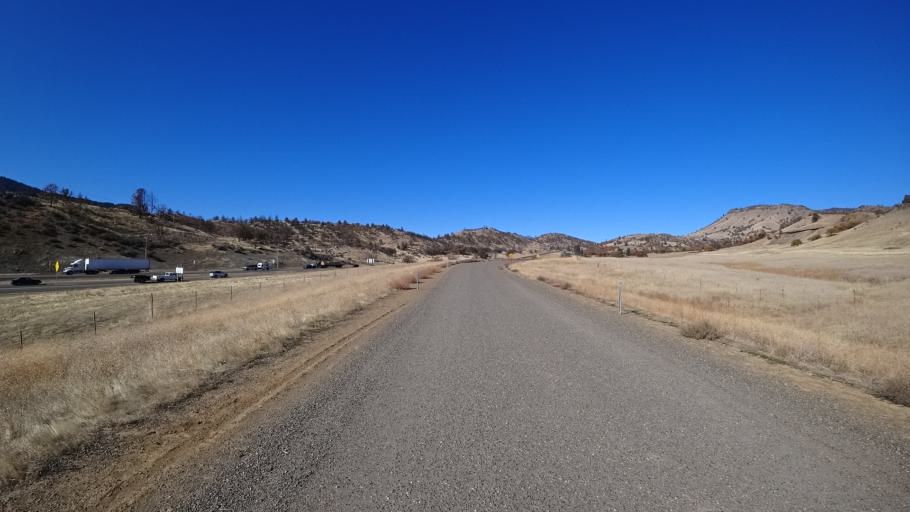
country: US
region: California
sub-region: Siskiyou County
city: Yreka
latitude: 41.9571
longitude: -122.5926
